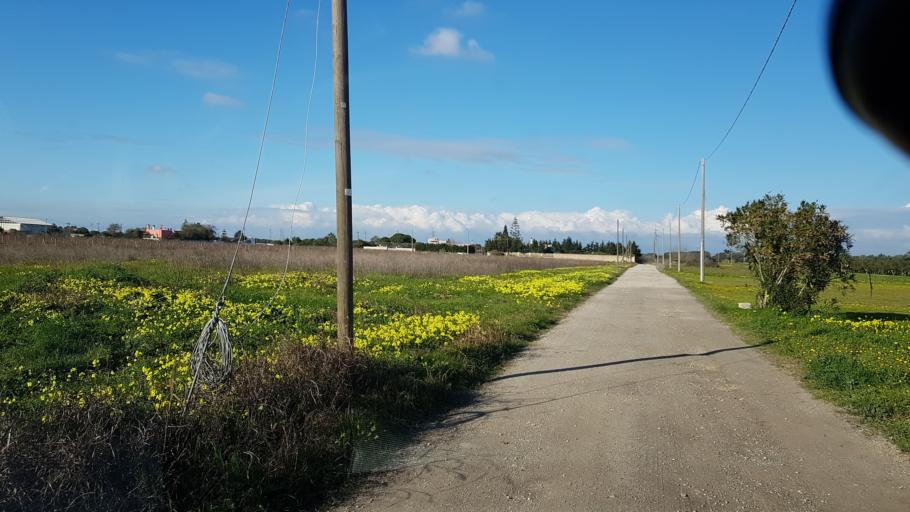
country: IT
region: Apulia
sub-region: Provincia di Brindisi
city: Tuturano
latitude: 40.5418
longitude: 17.9587
